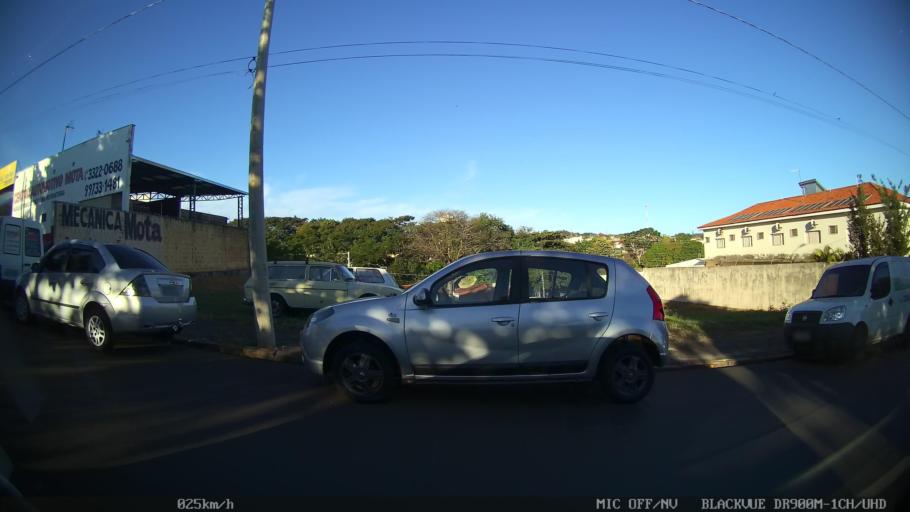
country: BR
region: Sao Paulo
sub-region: Araraquara
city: Araraquara
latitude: -21.8079
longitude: -48.1766
